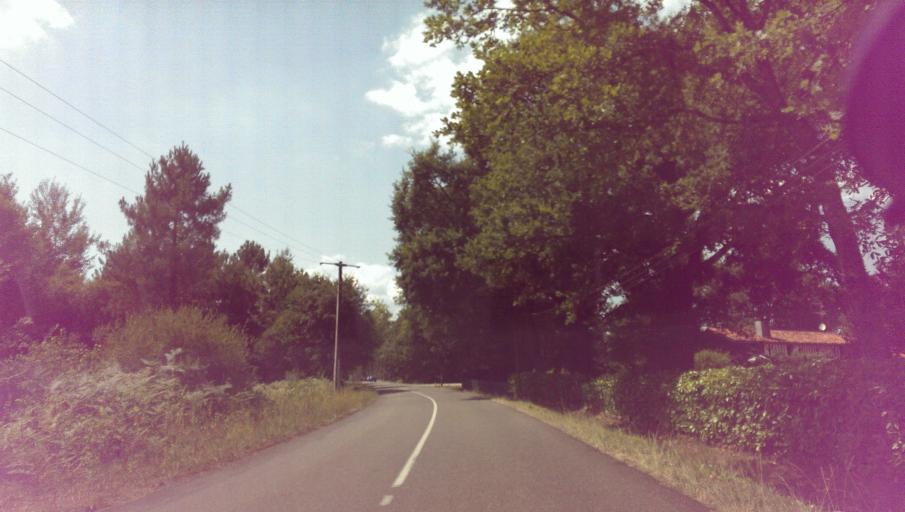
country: FR
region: Aquitaine
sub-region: Departement des Landes
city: Sabres
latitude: 44.1075
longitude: -0.5555
